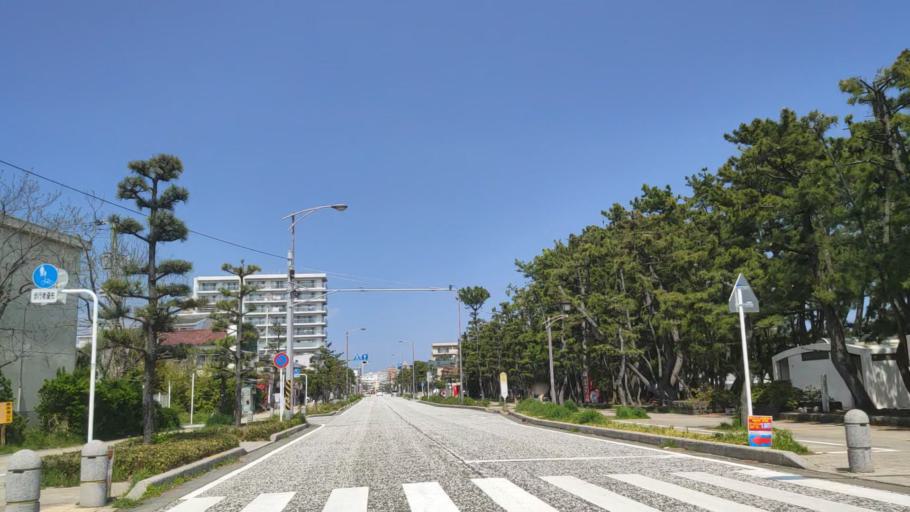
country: JP
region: Kanagawa
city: Hiratsuka
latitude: 35.3172
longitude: 139.3538
